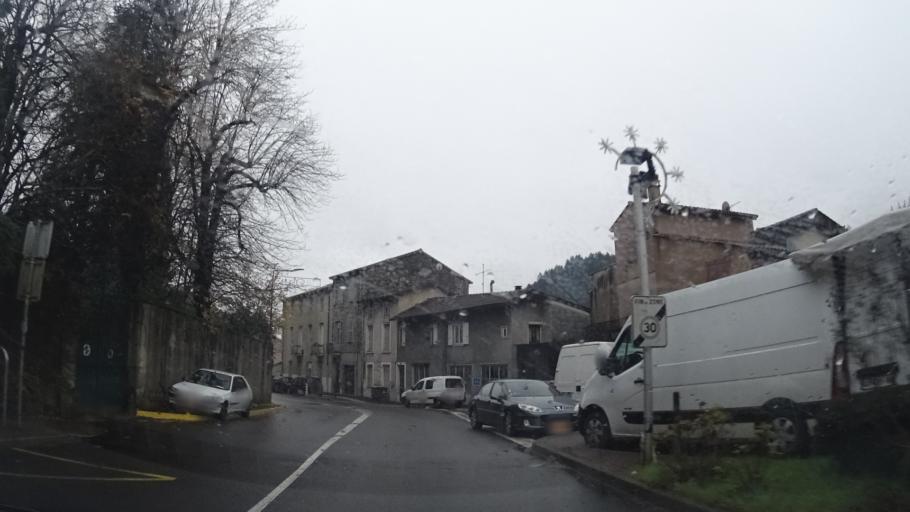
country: FR
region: Rhone-Alpes
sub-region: Departement de l'Ardeche
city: Vals-les-Bains
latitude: 44.6658
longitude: 4.3661
